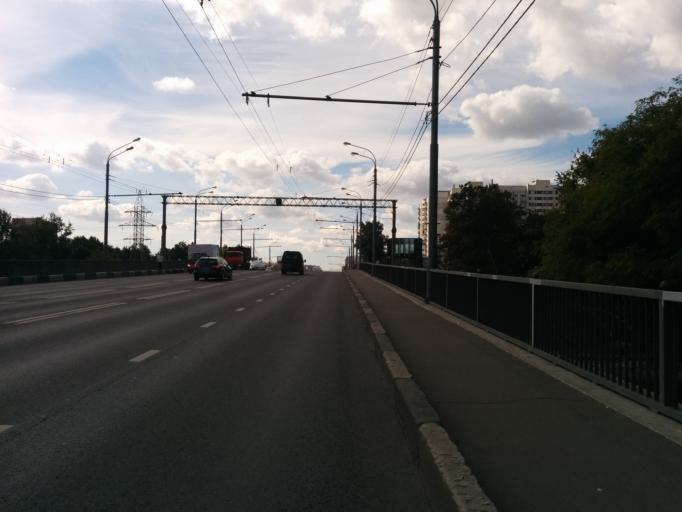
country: RU
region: Moscow
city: Mar'ina Roshcha
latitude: 55.8017
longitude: 37.6156
